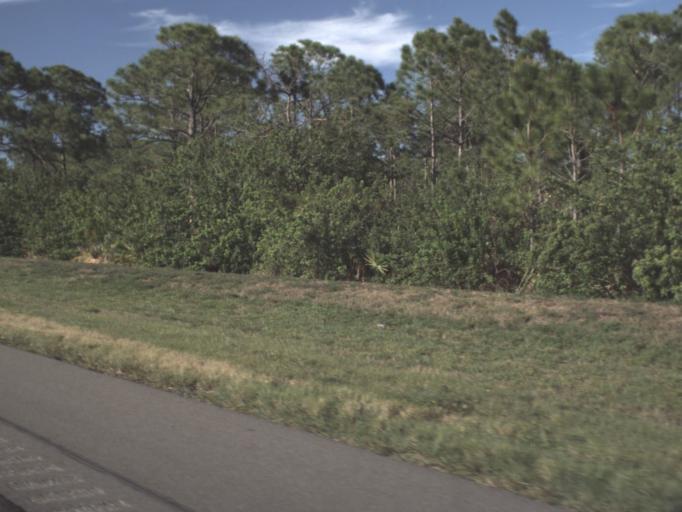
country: US
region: Florida
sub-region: Brevard County
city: Grant-Valkaria
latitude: 27.9207
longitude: -80.6011
